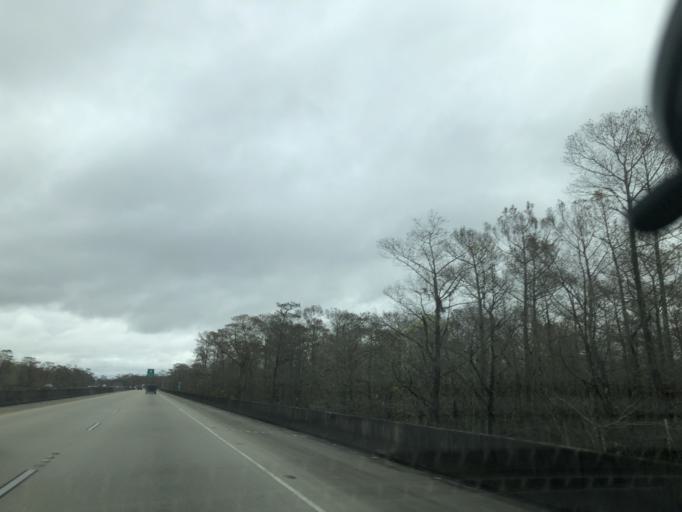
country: US
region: Louisiana
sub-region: Saint Charles Parish
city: Destrehan
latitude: 29.9651
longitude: -90.3435
